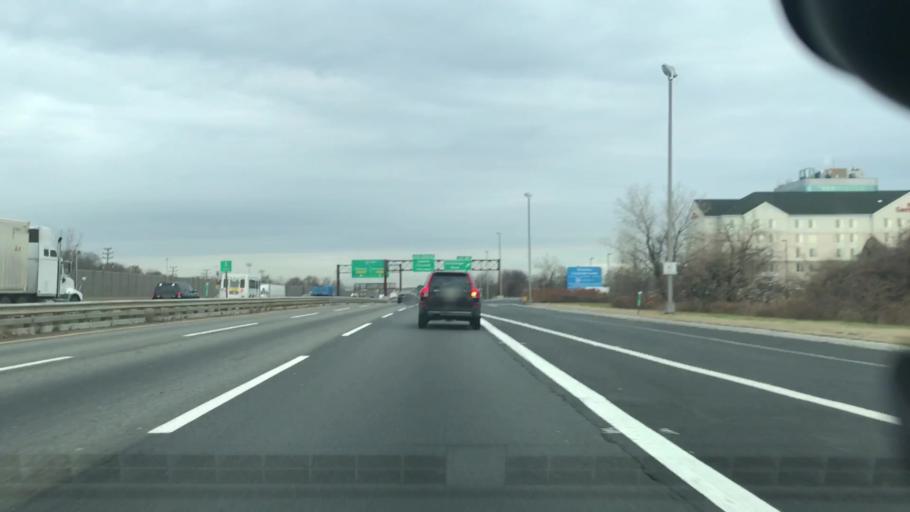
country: US
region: New Jersey
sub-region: Bergen County
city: Ridgefield Park
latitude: 40.8509
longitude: -74.0154
